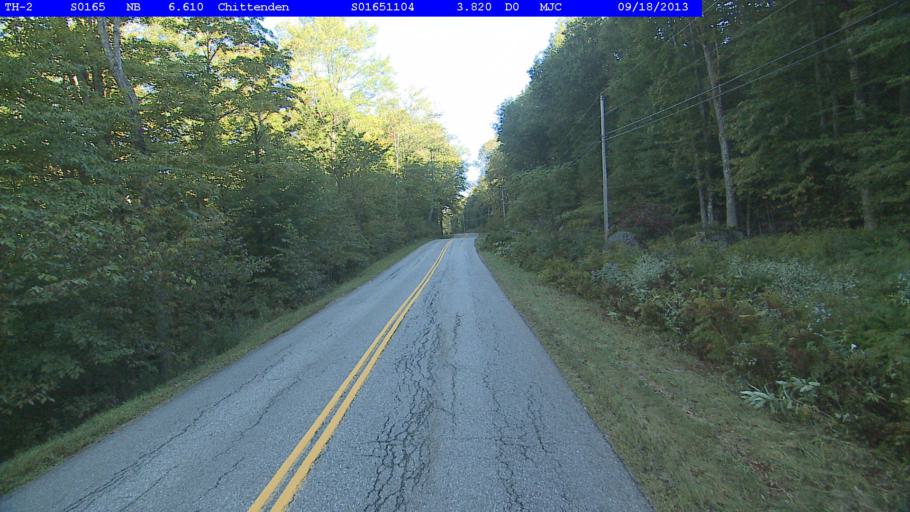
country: US
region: Vermont
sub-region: Rutland County
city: Rutland
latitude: 43.7290
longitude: -72.9708
